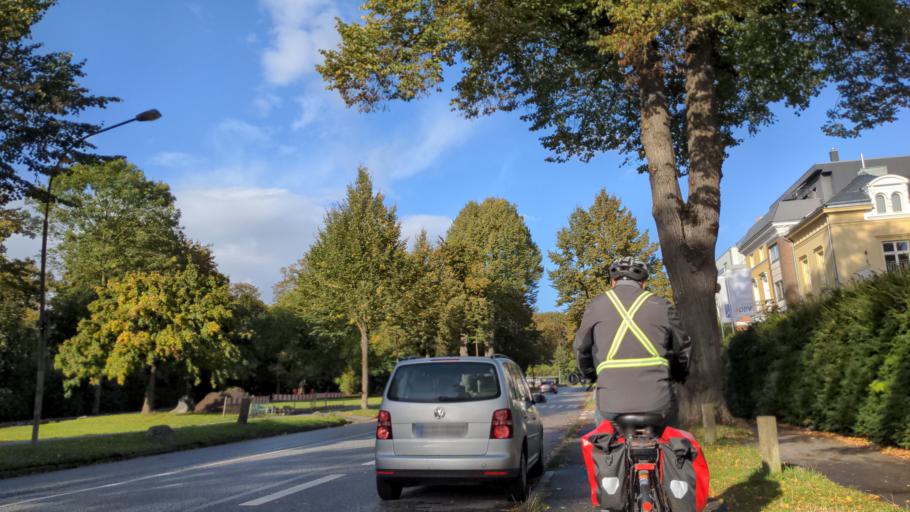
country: DE
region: Schleswig-Holstein
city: Luebeck
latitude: 53.8568
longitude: 10.6901
